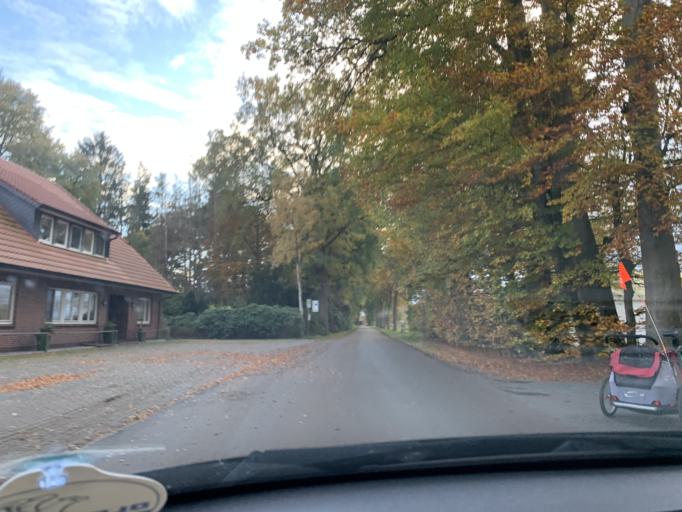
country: DE
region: Lower Saxony
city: Wiefelstede
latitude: 53.2651
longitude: 8.0703
